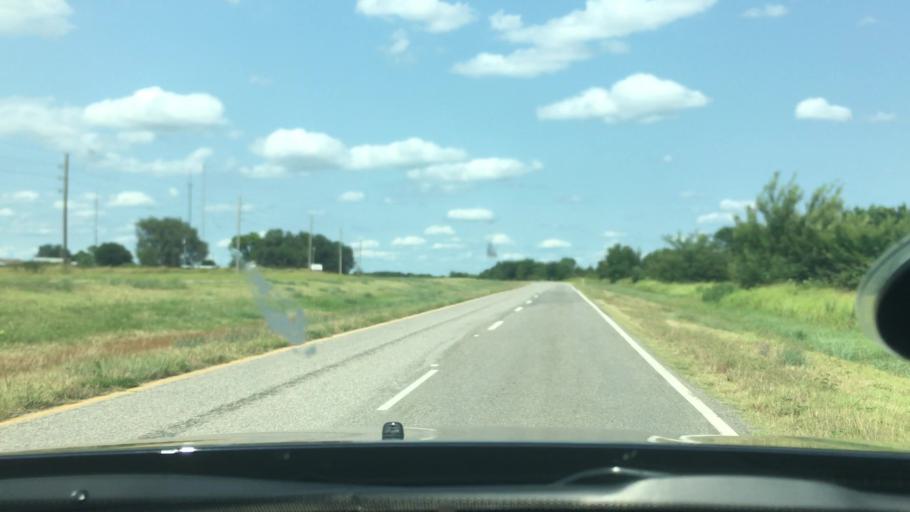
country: US
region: Oklahoma
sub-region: Pontotoc County
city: Ada
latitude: 34.7191
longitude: -96.7192
